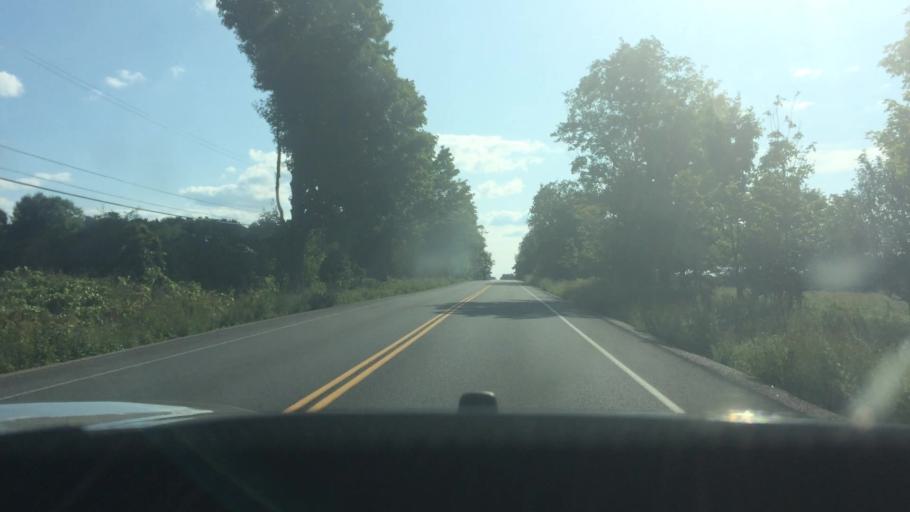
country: US
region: New York
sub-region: Franklin County
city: Malone
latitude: 44.7783
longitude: -74.5007
